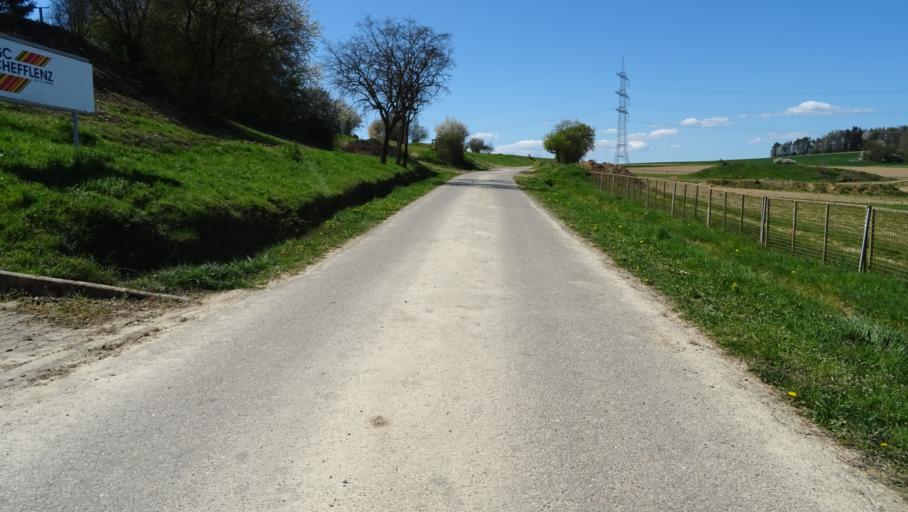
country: DE
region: Baden-Wuerttemberg
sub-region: Karlsruhe Region
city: Billigheim
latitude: 49.3939
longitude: 9.2530
